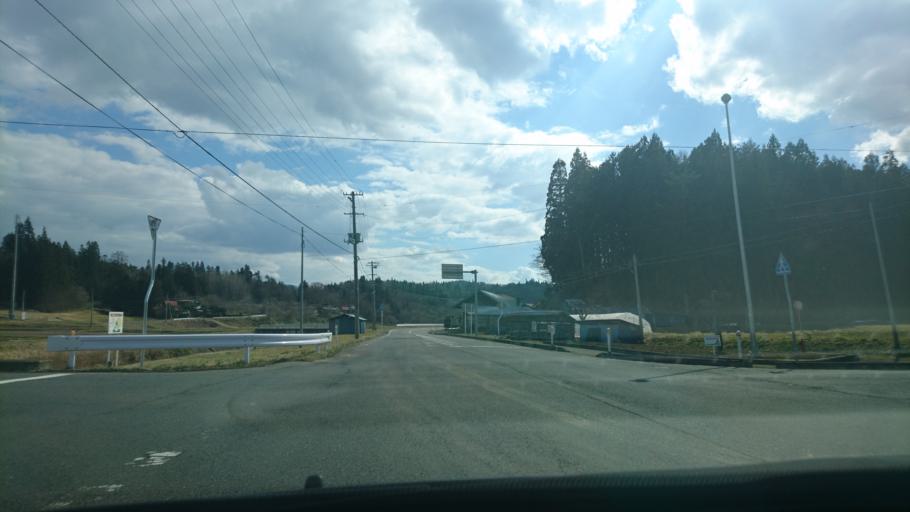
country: JP
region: Iwate
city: Hanamaki
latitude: 39.3457
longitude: 141.2395
